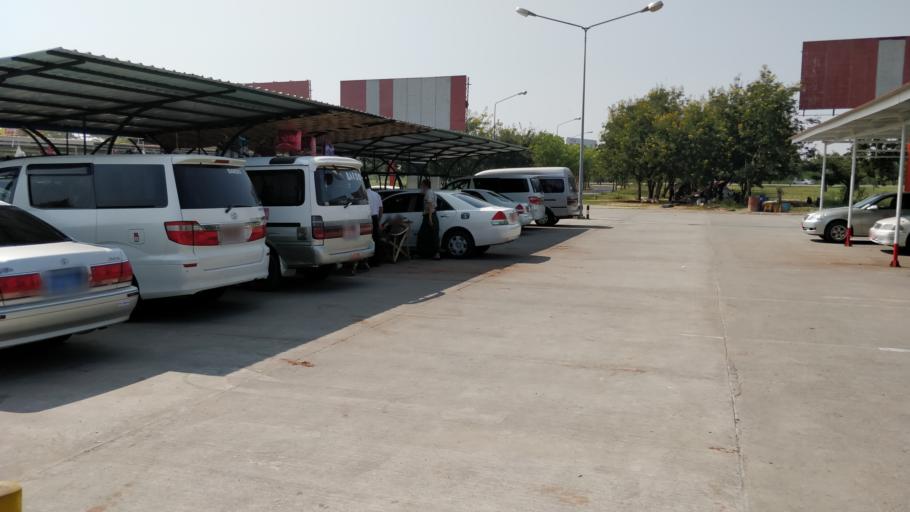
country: MM
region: Sagain
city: Sagaing
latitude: 21.7062
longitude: 95.9684
